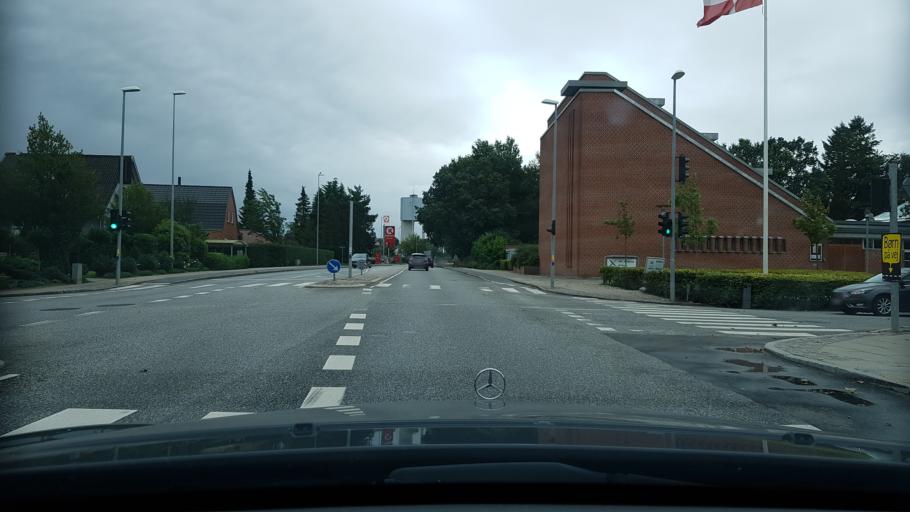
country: DK
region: Central Jutland
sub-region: Randers Kommune
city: Randers
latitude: 56.4772
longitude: 10.0411
